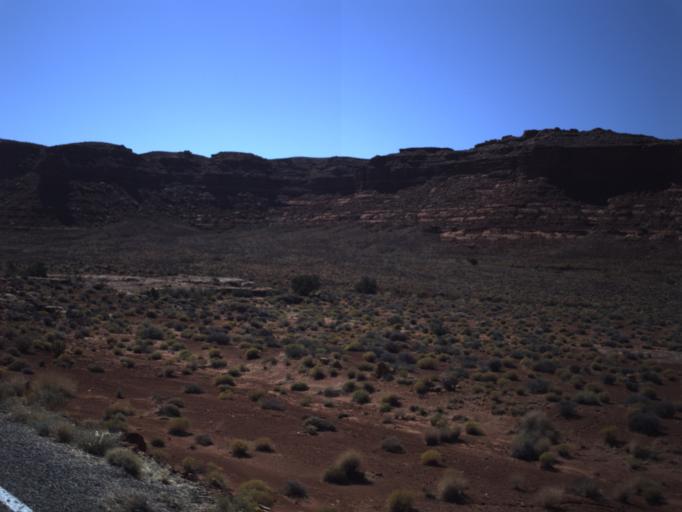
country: US
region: Utah
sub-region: San Juan County
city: Blanding
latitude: 37.8133
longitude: -110.3428
